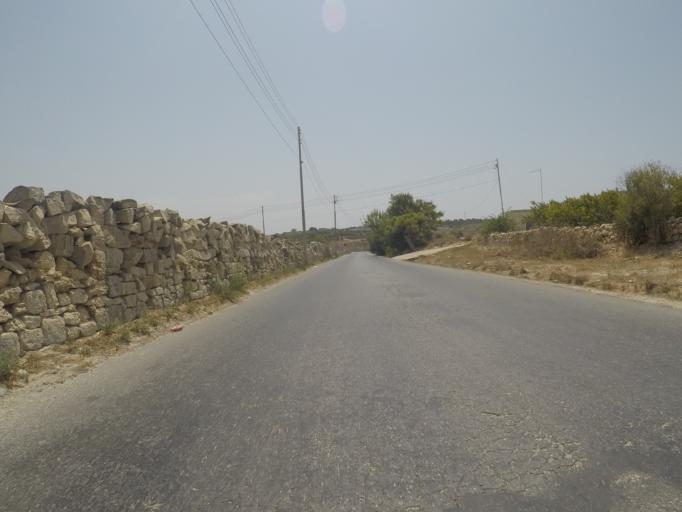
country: MT
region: Is-Siggiewi
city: Siggiewi
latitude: 35.8599
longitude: 14.4198
